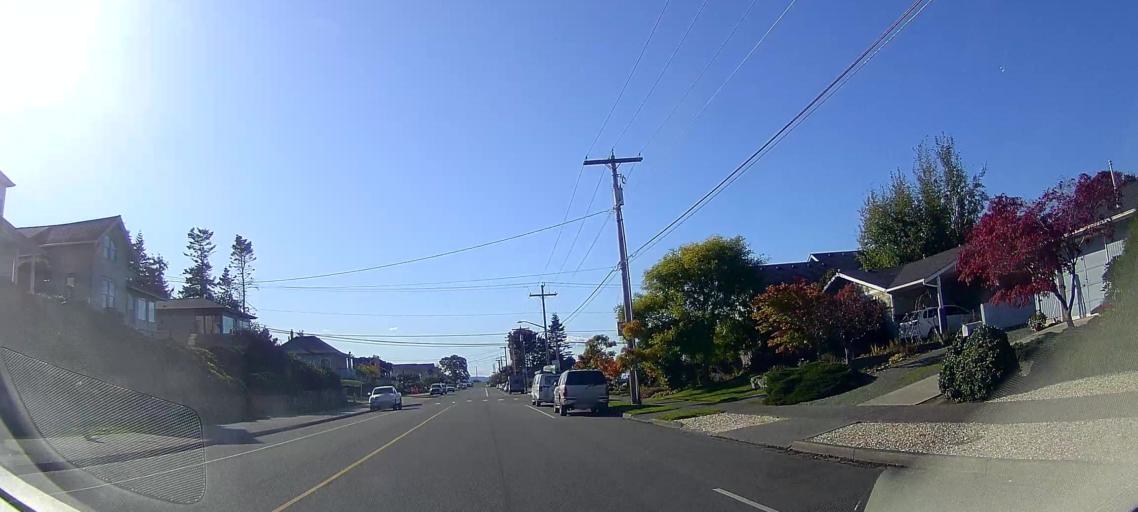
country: US
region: Washington
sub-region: Skagit County
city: Anacortes
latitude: 48.5175
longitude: -122.6195
